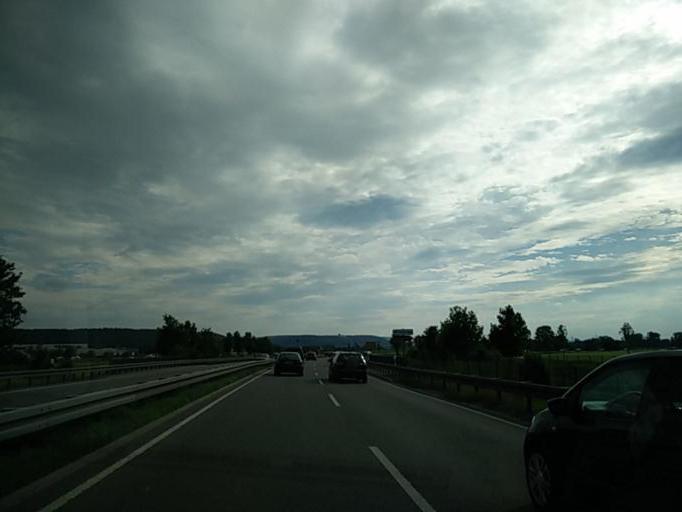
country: DE
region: Baden-Wuerttemberg
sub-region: Tuebingen Region
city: Tuebingen
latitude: 48.5023
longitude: 9.0353
